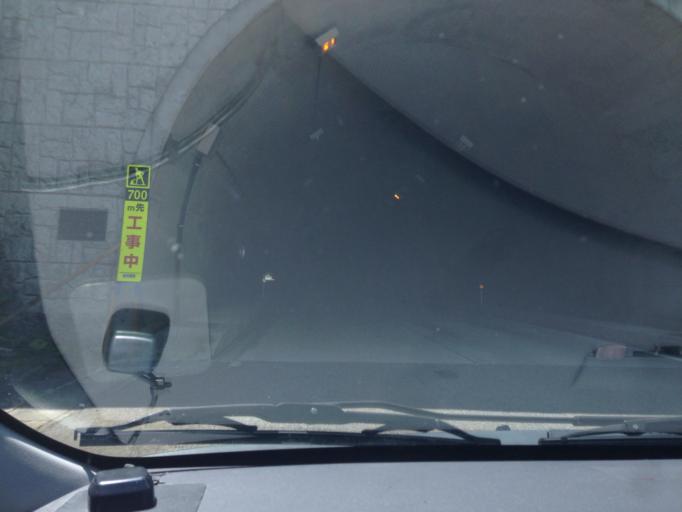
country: JP
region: Fukushima
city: Kitakata
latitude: 37.2589
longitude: 139.7134
